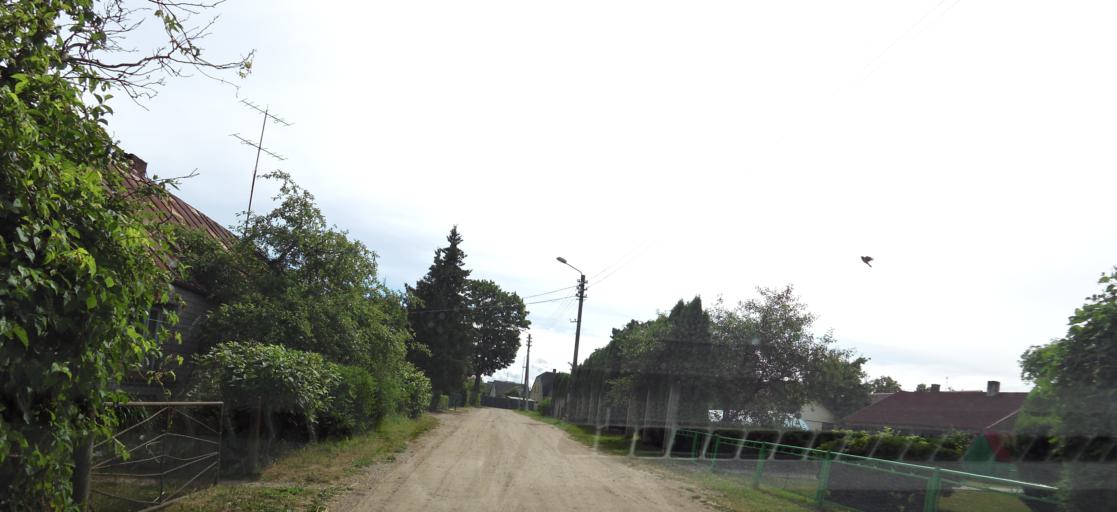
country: LT
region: Panevezys
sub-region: Birzai
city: Birzai
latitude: 56.2018
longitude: 24.7652
